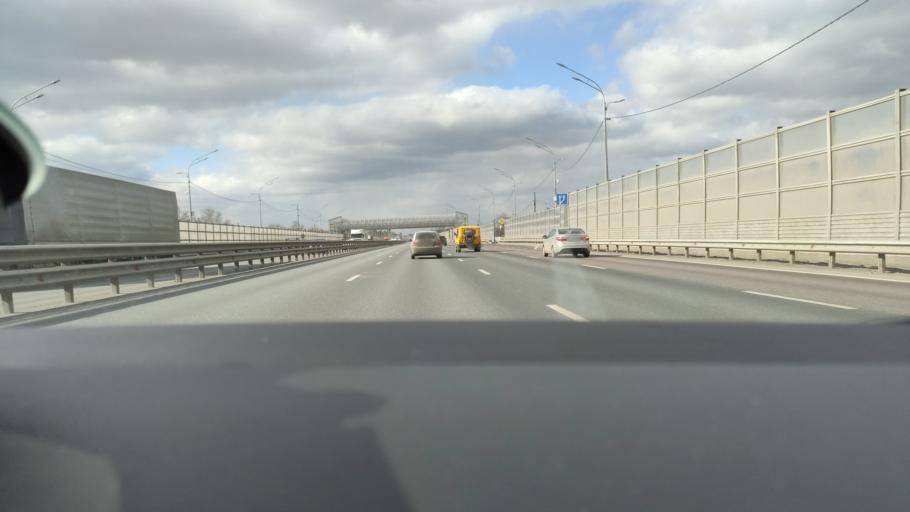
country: RU
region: Moskovskaya
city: Chornaya
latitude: 55.8051
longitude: 38.0453
